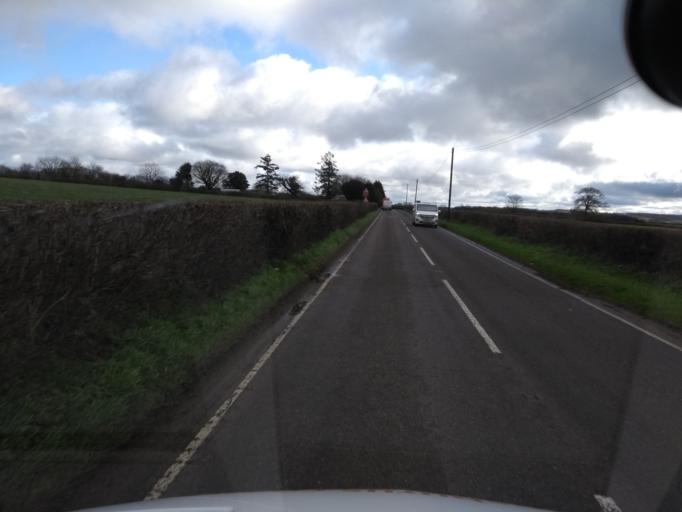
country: GB
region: England
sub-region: Dorset
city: Sherborne
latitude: 50.9310
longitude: -2.5063
